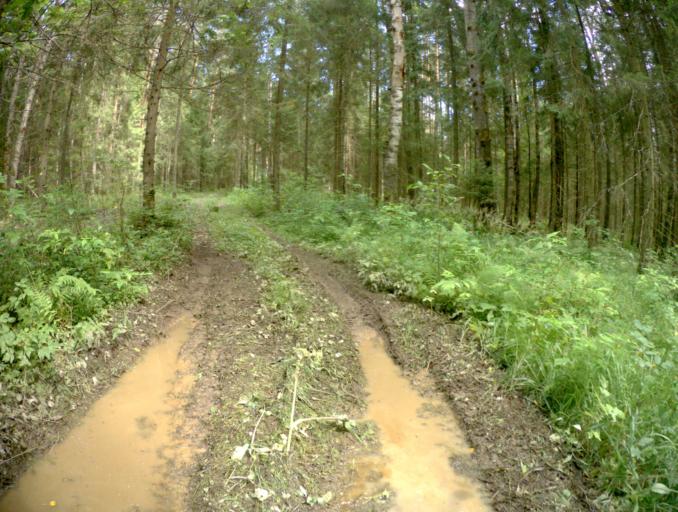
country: RU
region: Vladimir
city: Orgtrud
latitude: 56.0738
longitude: 40.6397
